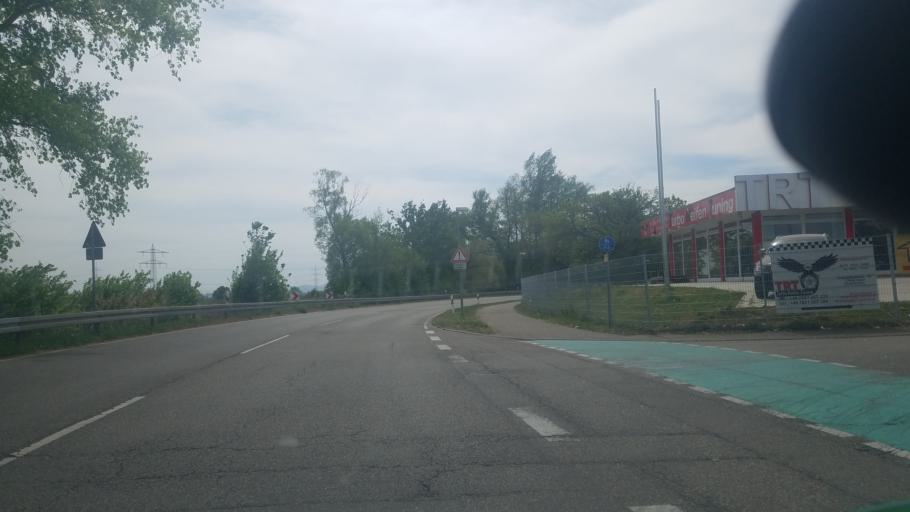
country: DE
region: Baden-Wuerttemberg
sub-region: Freiburg Region
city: Kehl
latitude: 48.5524
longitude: 7.8434
